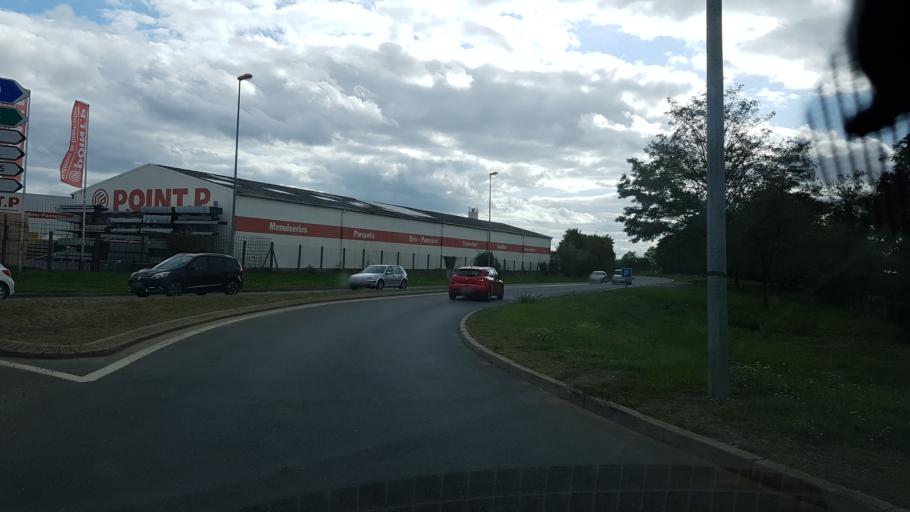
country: FR
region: Centre
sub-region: Departement du Loiret
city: Pithiviers
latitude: 48.1870
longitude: 2.2408
